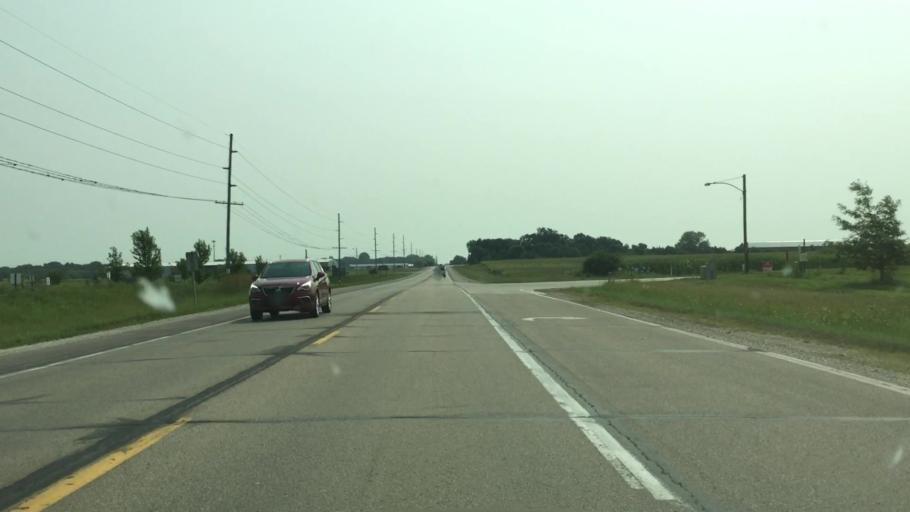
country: US
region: Iowa
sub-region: Dickinson County
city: Milford
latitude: 43.3424
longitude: -95.1656
